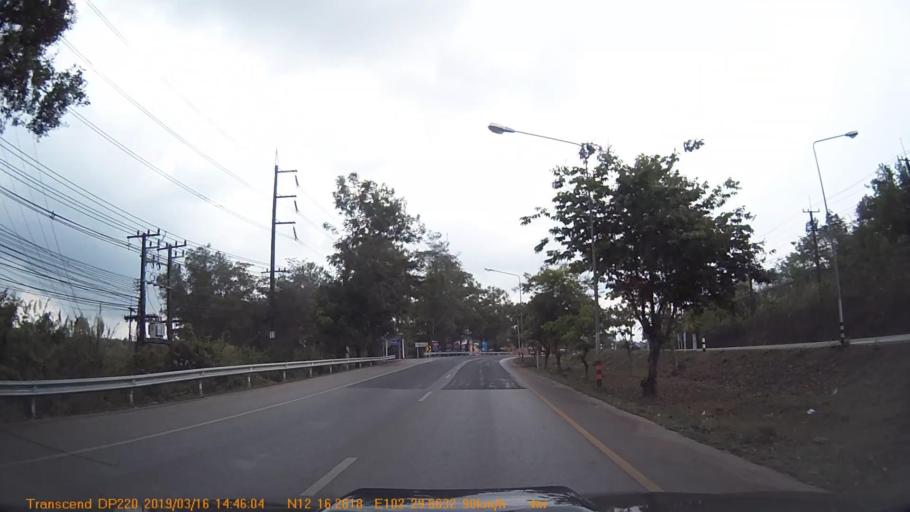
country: TH
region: Trat
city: Trat
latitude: 12.2715
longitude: 102.4943
